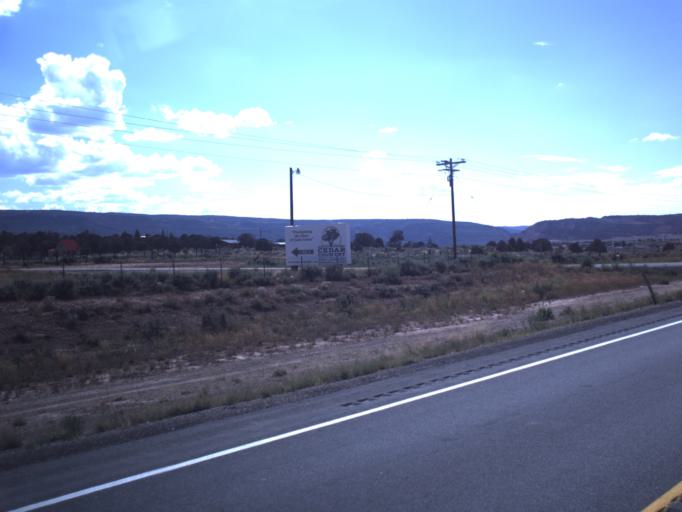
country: US
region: Utah
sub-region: Duchesne County
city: Duchesne
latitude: 40.2091
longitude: -110.8250
